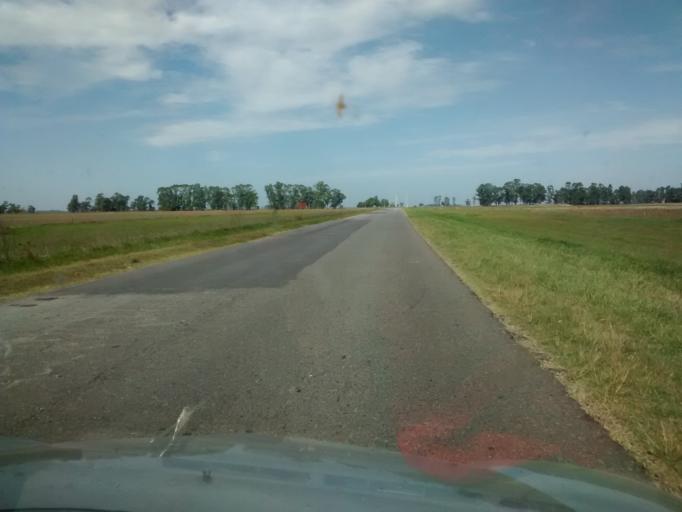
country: AR
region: Buenos Aires
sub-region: Partido de Ayacucho
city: Ayacucho
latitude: -37.2208
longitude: -58.4984
